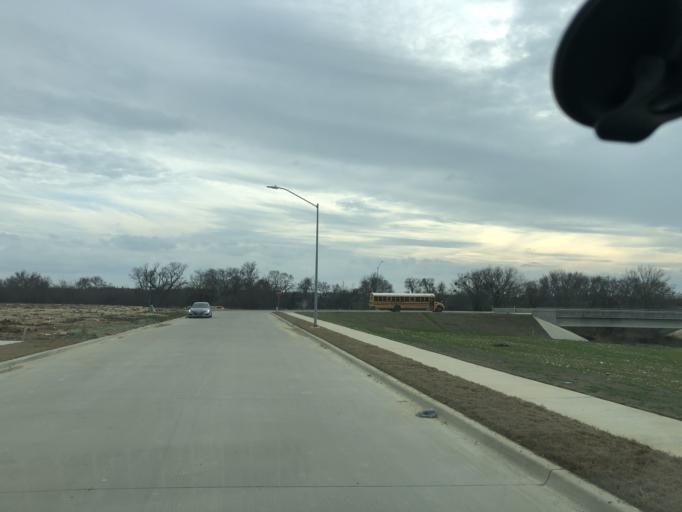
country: US
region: Texas
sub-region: Tarrant County
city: Saginaw
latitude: 32.9039
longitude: -97.3699
